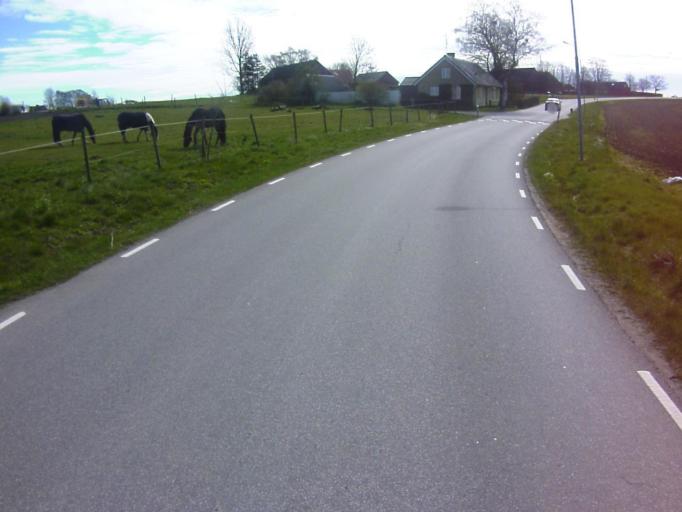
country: SE
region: Skane
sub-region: Kavlinge Kommun
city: Hofterup
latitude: 55.7874
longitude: 12.9734
